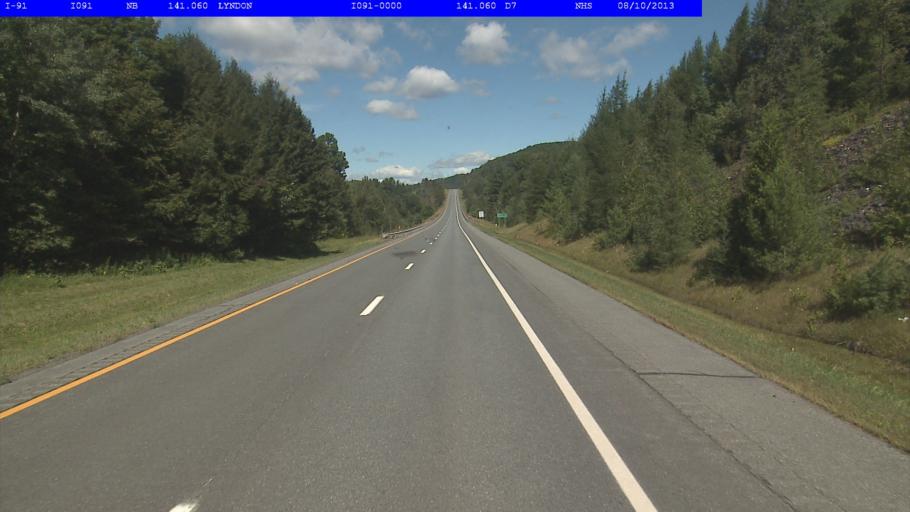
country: US
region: Vermont
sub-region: Caledonia County
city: Lyndonville
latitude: 44.5683
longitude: -72.0350
